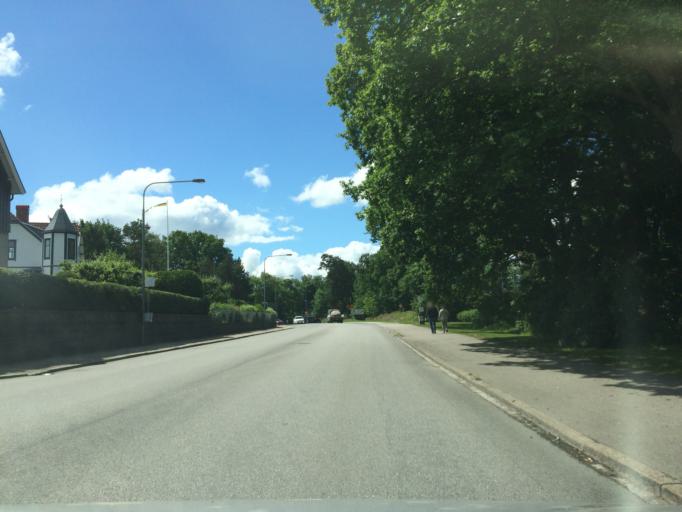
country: SE
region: Vaestra Goetaland
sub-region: Trollhattan
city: Trollhattan
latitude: 58.2911
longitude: 12.2984
